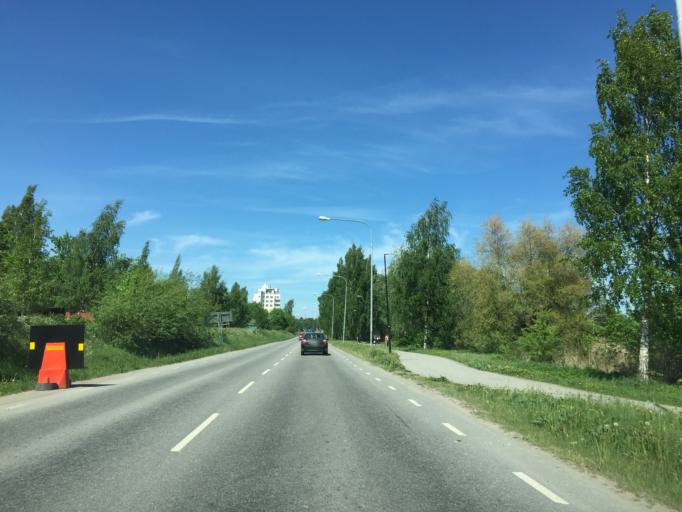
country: SE
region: OErebro
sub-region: Orebro Kommun
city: Orebro
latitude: 59.2687
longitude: 15.2407
